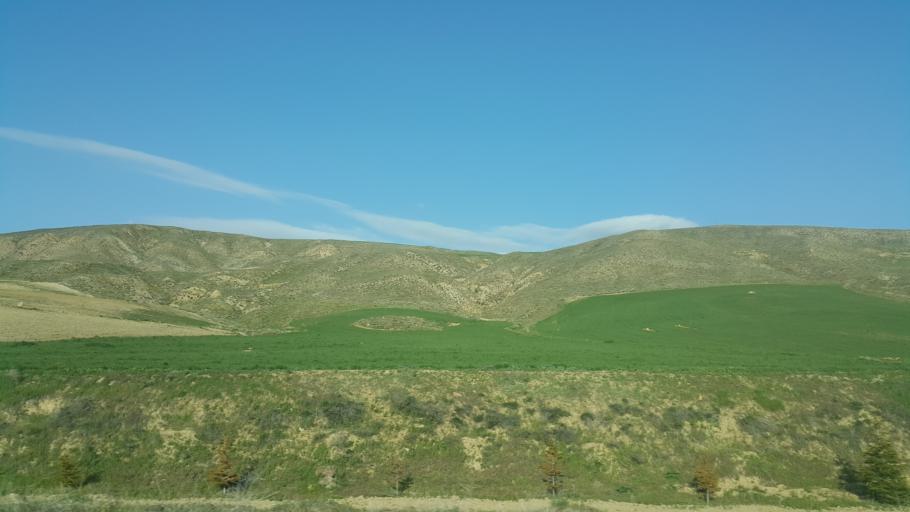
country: TR
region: Ankara
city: Sereflikochisar
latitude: 39.0280
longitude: 33.4477
